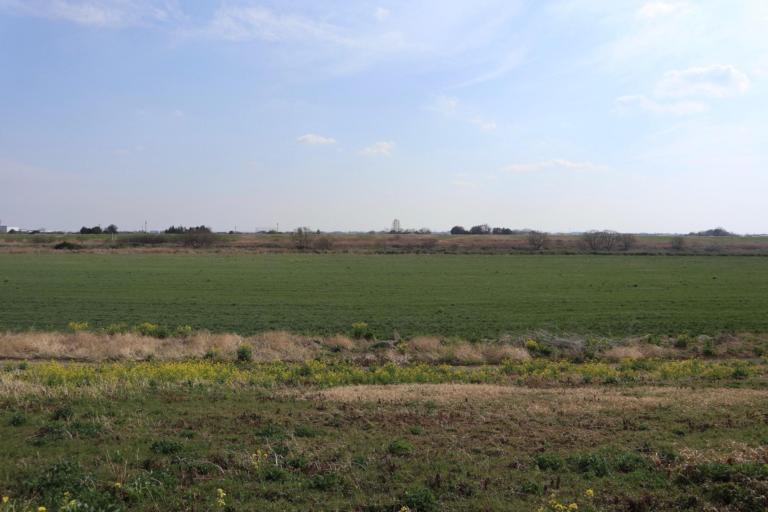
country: JP
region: Tochigi
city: Sano
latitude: 36.2711
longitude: 139.5908
